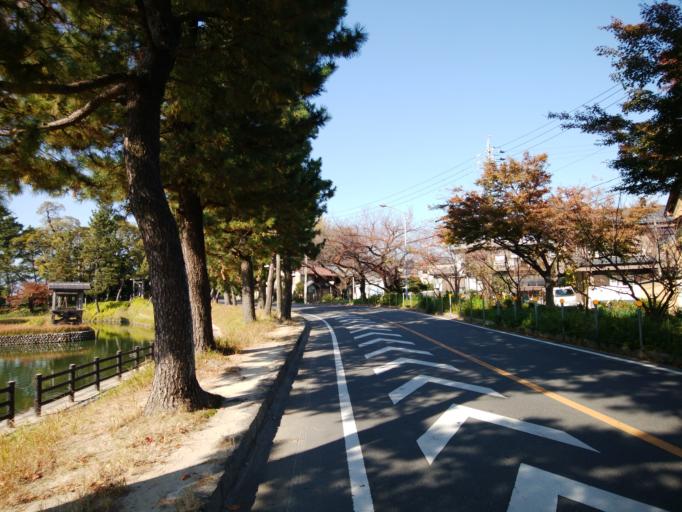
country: JP
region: Aichi
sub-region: Tsushima-shi
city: Tsushima
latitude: 35.1744
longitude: 136.7240
